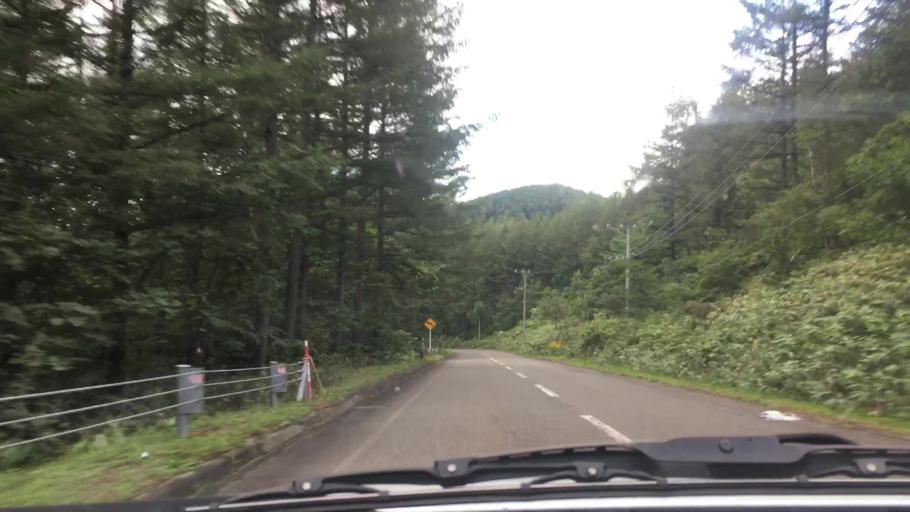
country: JP
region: Hokkaido
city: Otofuke
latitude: 43.1541
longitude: 142.8580
